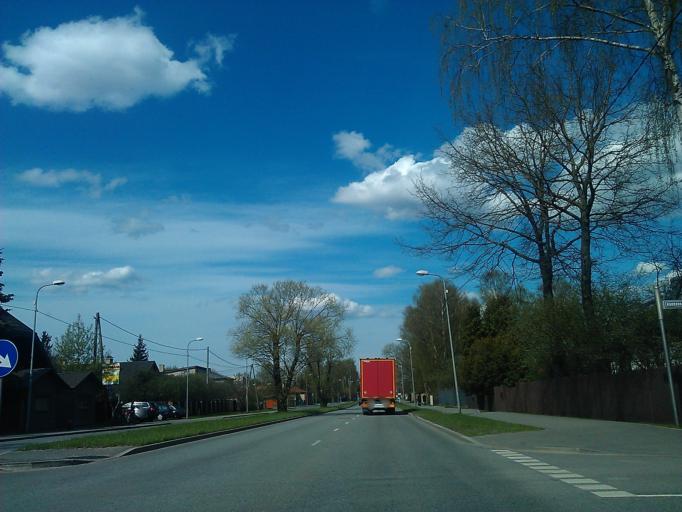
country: LV
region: Riga
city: Riga
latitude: 56.9435
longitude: 24.1826
